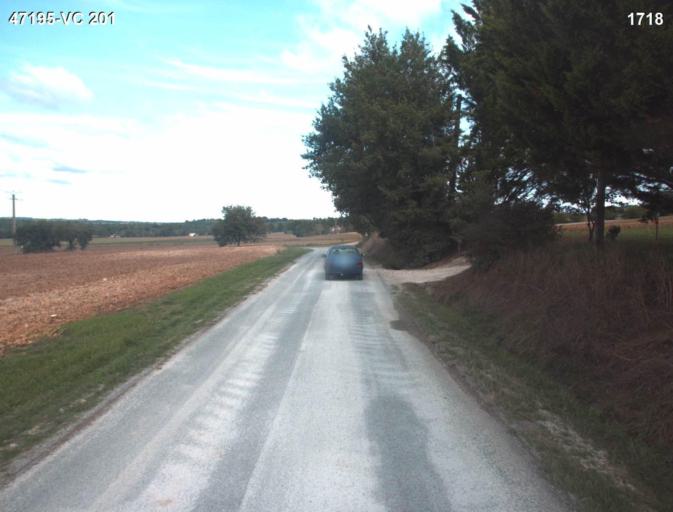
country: FR
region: Aquitaine
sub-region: Departement du Lot-et-Garonne
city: Barbaste
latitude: 44.1319
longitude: 0.2993
